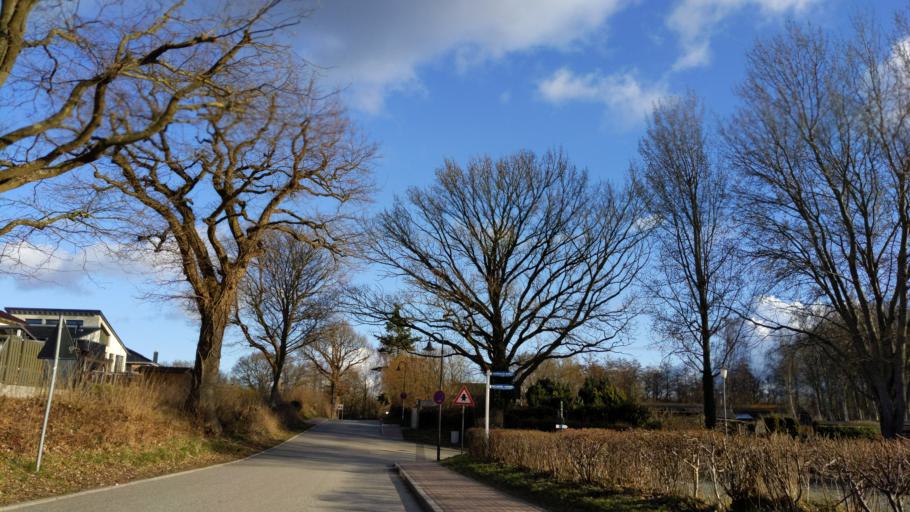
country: DE
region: Schleswig-Holstein
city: Scharbeutz
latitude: 54.0300
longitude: 10.7419
